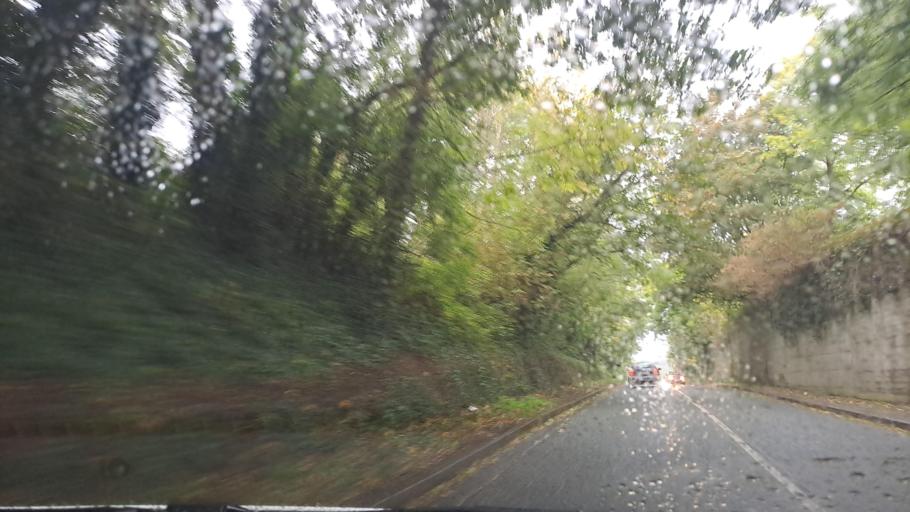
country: IE
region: Leinster
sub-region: Lu
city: Dundalk
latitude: 53.9976
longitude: -6.4313
